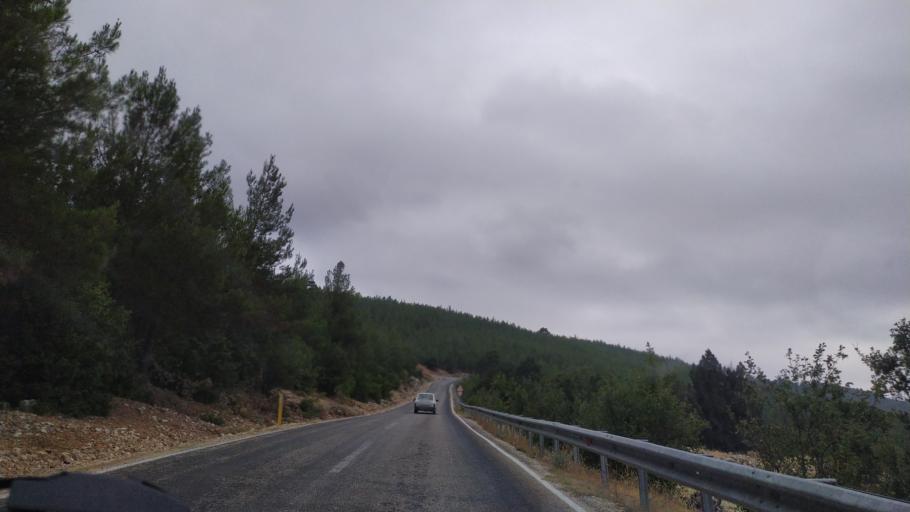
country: TR
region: Mersin
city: Silifke
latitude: 36.5423
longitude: 33.9317
